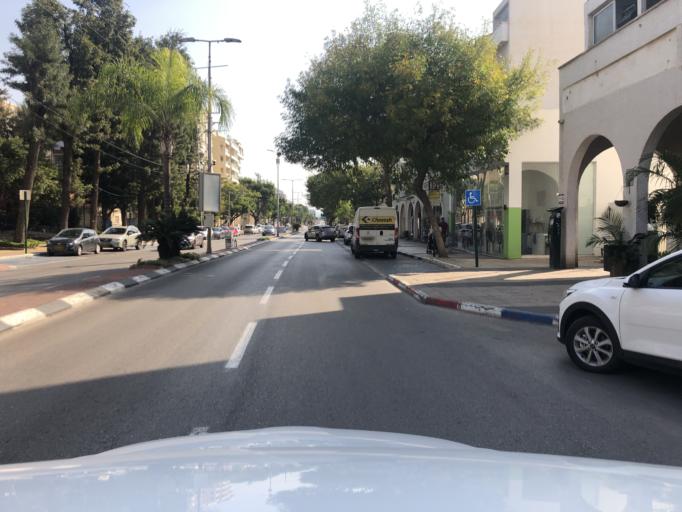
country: IL
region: Central District
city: Kfar Saba
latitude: 32.1745
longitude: 34.9116
